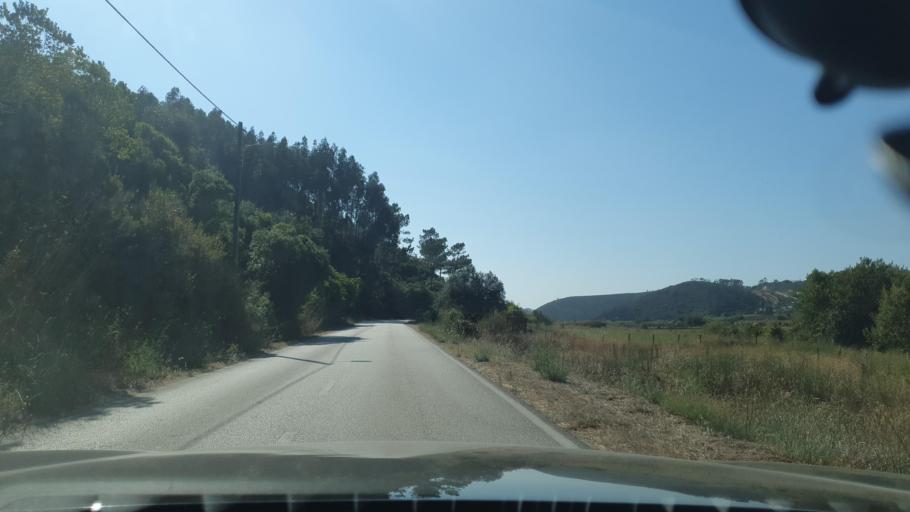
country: PT
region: Beja
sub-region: Odemira
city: Sao Teotonio
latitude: 37.4311
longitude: -8.7778
